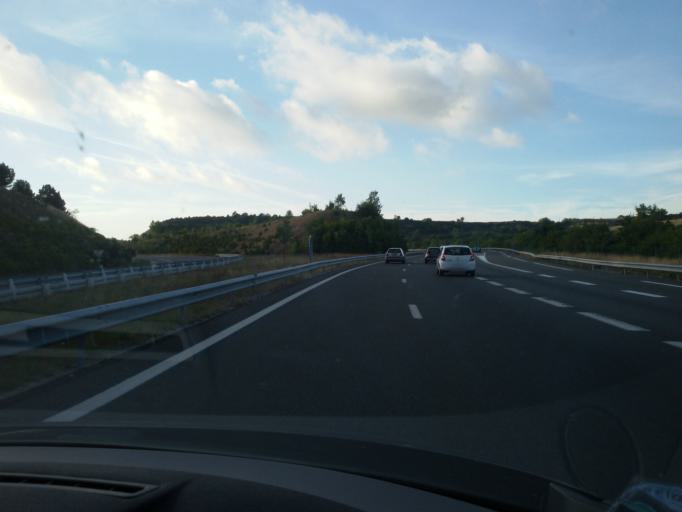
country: FR
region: Languedoc-Roussillon
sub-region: Departement de l'Herault
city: Lodeve
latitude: 43.8439
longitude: 3.3122
